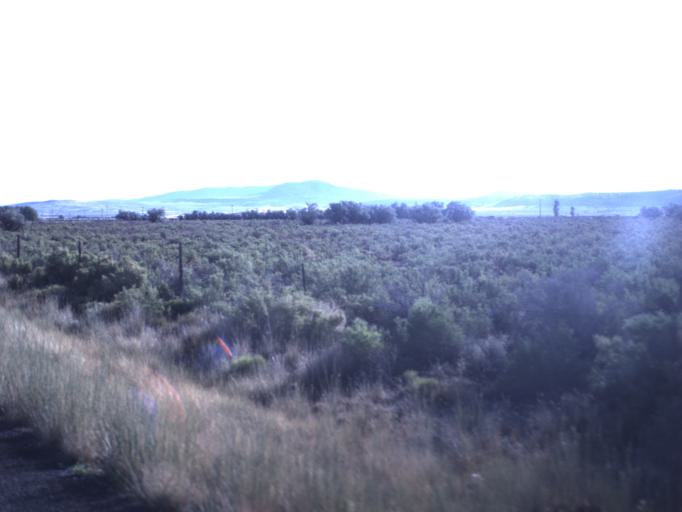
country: US
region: Utah
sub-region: Iron County
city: Enoch
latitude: 37.7802
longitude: -113.0551
